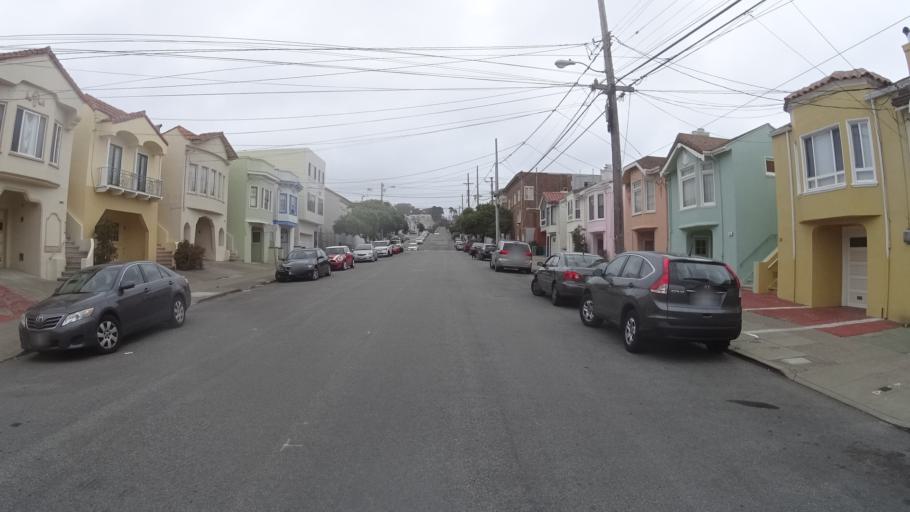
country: US
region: California
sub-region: San Mateo County
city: Daly City
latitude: 37.7747
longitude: -122.4983
